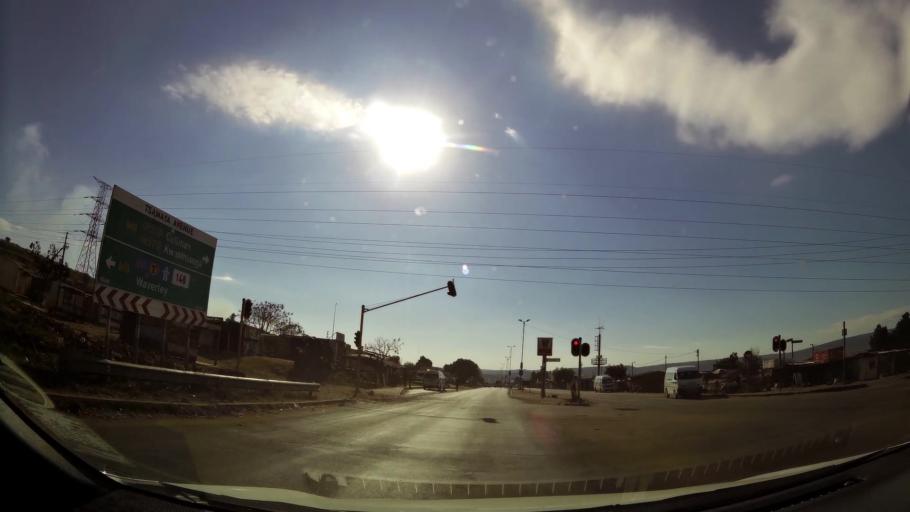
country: ZA
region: Gauteng
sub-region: City of Tshwane Metropolitan Municipality
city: Cullinan
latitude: -25.7031
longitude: 28.3934
